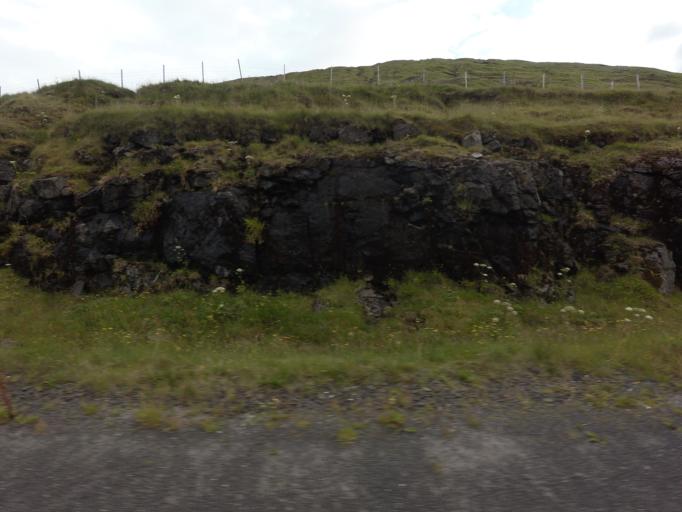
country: FO
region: Streymoy
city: Kollafjordhur
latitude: 62.1648
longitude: -6.9509
